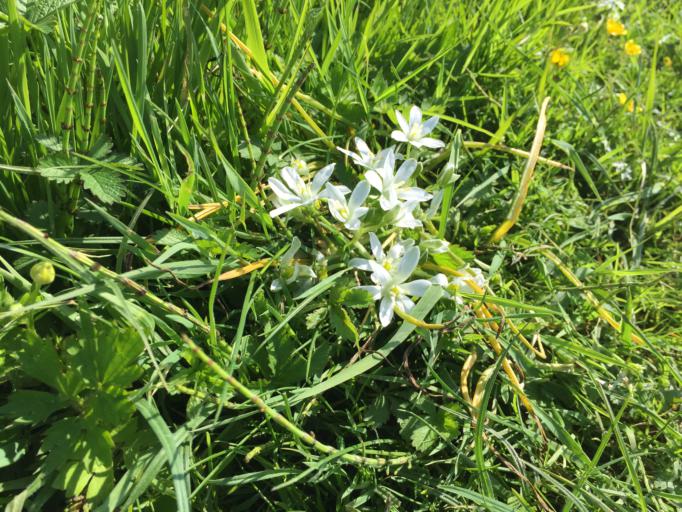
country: DK
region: Zealand
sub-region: Lolland Kommune
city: Maribo
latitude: 54.8954
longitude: 11.3610
